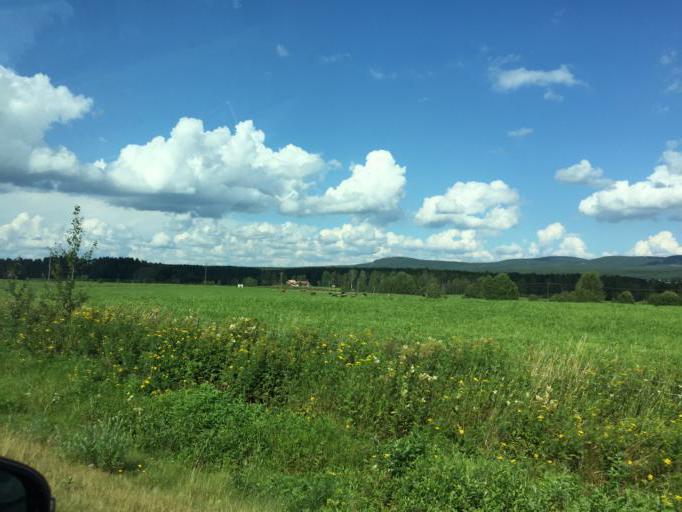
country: SE
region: Gaevleborg
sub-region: Bollnas Kommun
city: Arbra
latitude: 61.4491
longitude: 16.3848
